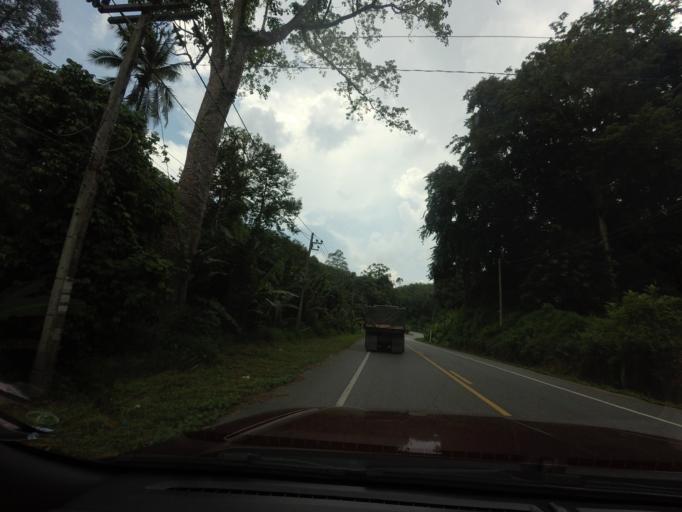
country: TH
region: Yala
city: Than To
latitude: 6.0820
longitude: 101.1851
